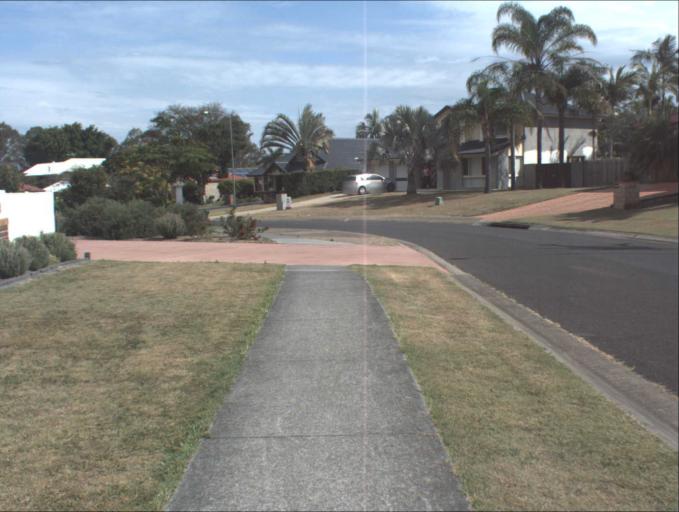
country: AU
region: Queensland
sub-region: Logan
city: Beenleigh
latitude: -27.6777
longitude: 153.2072
